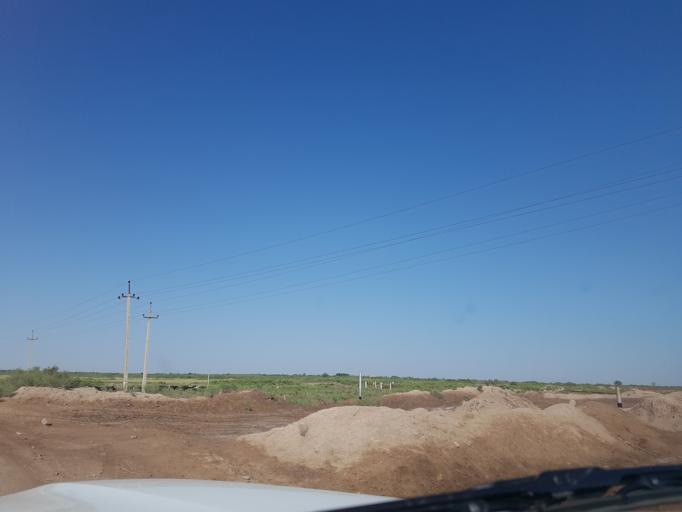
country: TM
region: Dasoguz
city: Koeneuergench
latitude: 42.1345
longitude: 58.9517
